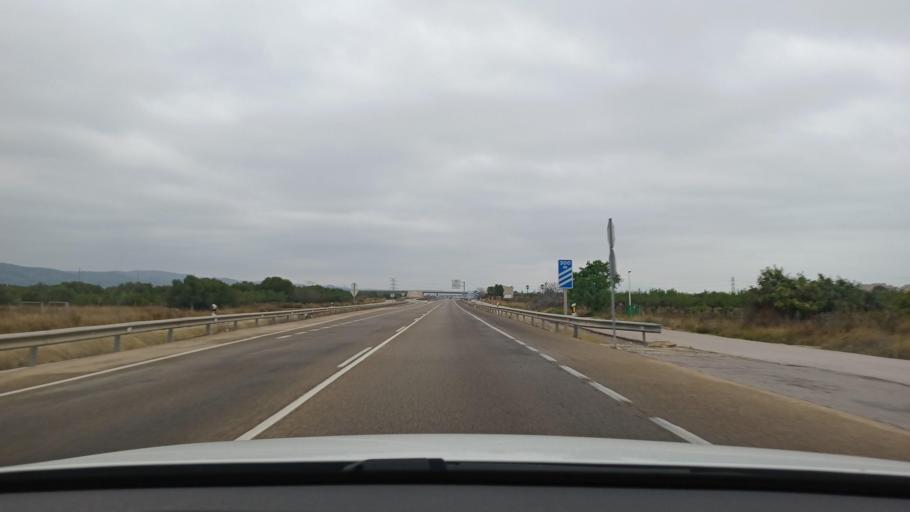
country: ES
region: Valencia
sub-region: Provincia de Castello
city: Orpesa/Oropesa del Mar
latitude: 40.1152
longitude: 0.1405
